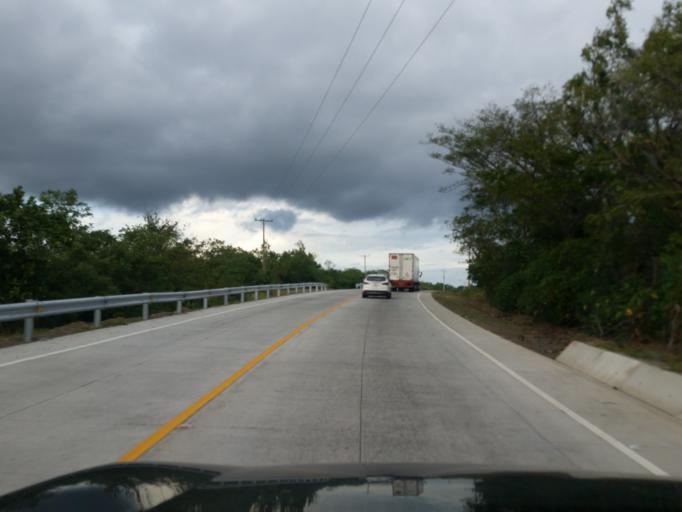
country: NI
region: Managua
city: Ciudad Sandino
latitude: 12.0831
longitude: -86.4077
